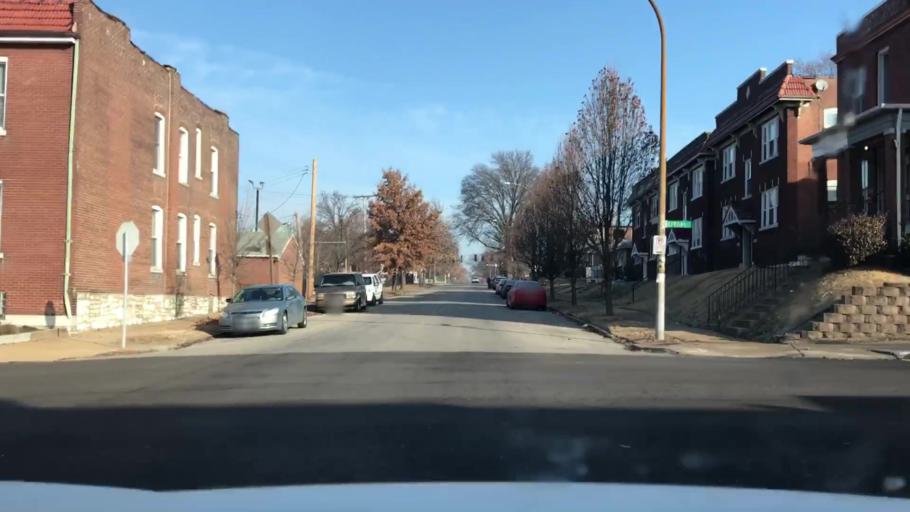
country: US
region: Missouri
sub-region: City of Saint Louis
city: St. Louis
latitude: 38.5965
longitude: -90.2365
